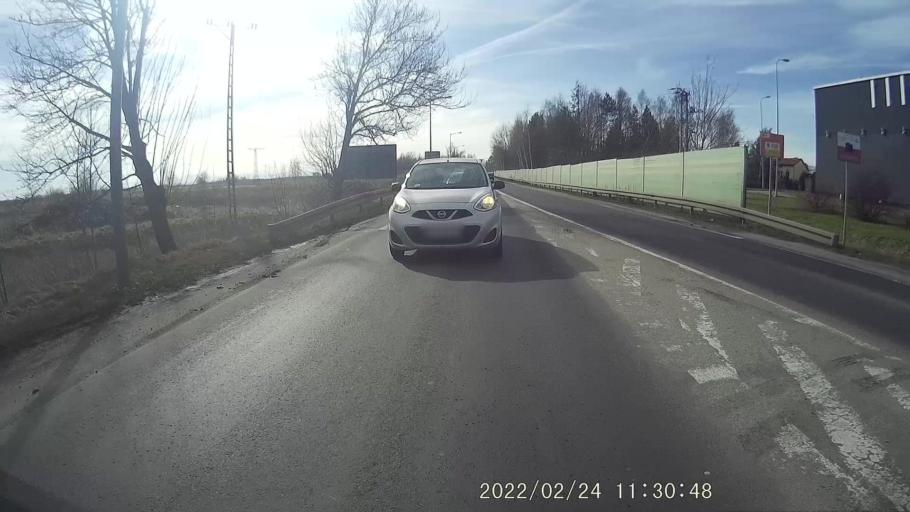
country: PL
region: Lower Silesian Voivodeship
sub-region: Powiat polkowicki
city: Przemkow
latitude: 51.5221
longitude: 15.7243
